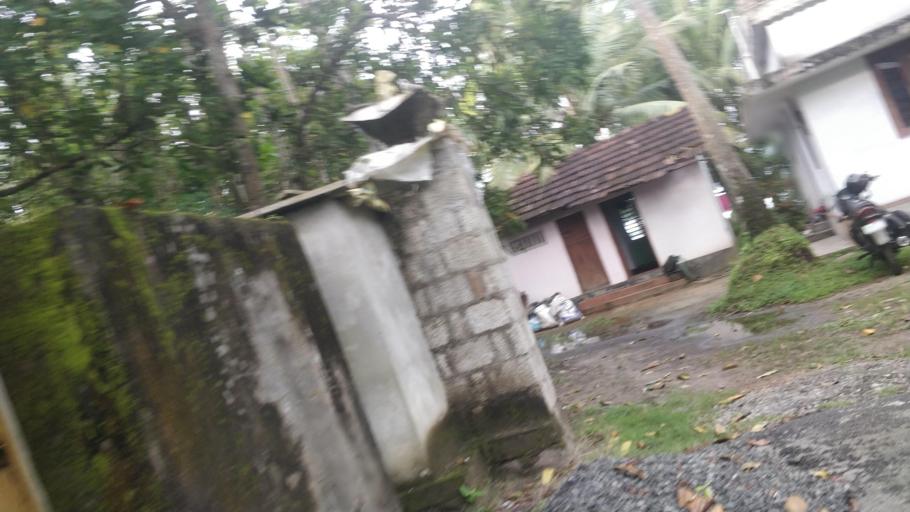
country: IN
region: Kerala
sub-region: Alappuzha
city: Shertallai
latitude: 9.6961
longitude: 76.3645
